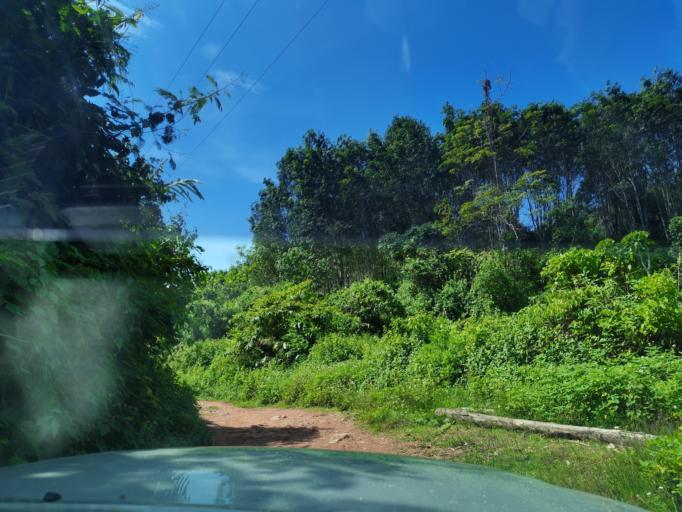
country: LA
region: Loungnamtha
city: Muang Nale
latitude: 20.5330
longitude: 101.0649
